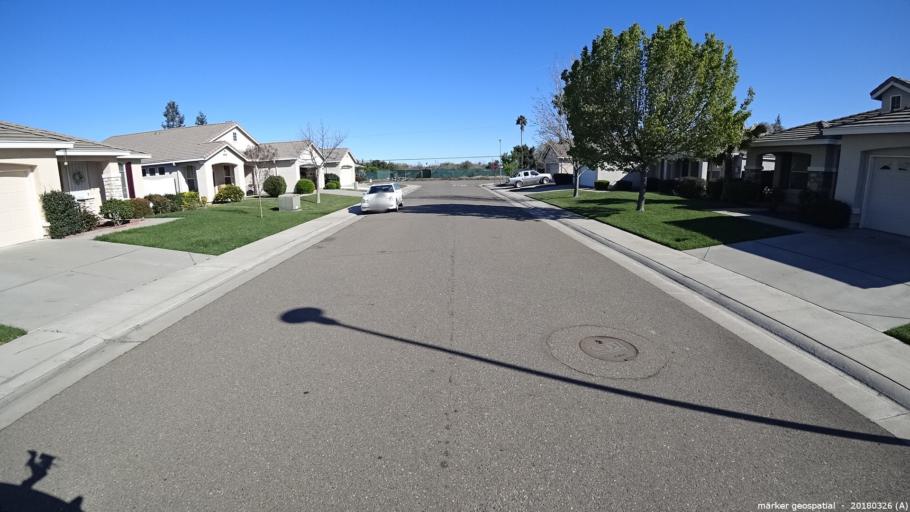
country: US
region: California
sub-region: Sacramento County
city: Florin
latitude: 38.4683
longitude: -121.4104
